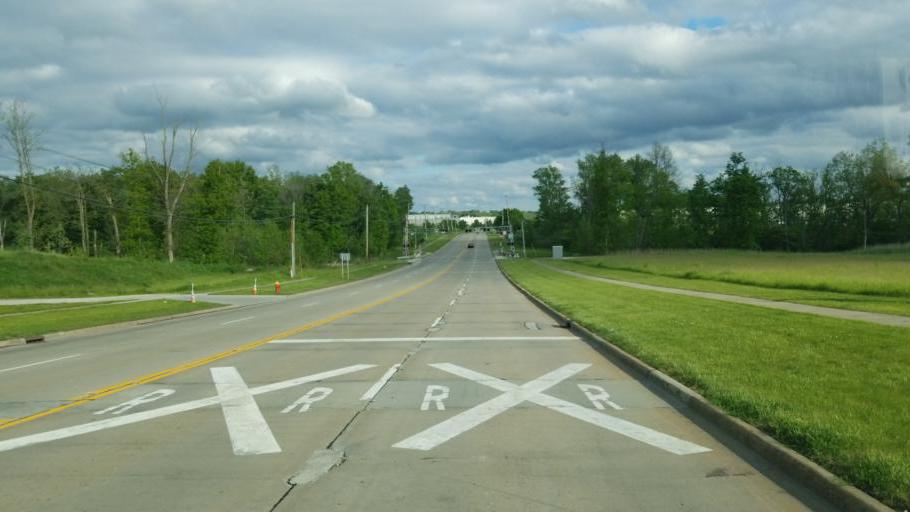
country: US
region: Ohio
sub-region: Cuyahoga County
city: Solon
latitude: 41.3631
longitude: -81.4684
